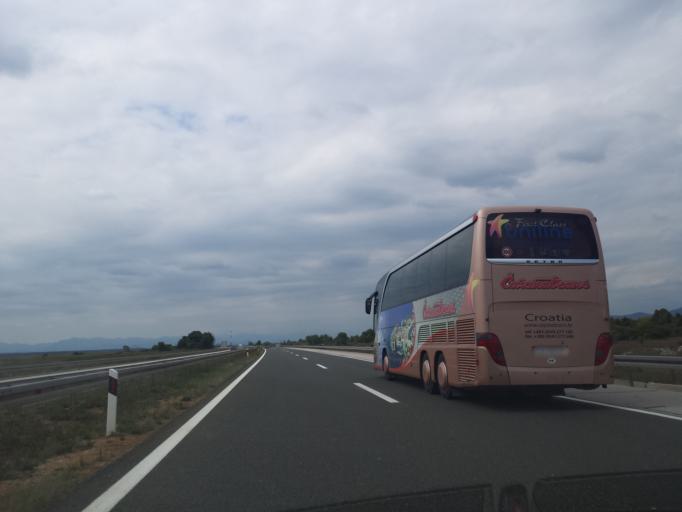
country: HR
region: Licko-Senjska
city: Gospic
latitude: 44.4744
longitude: 15.5818
